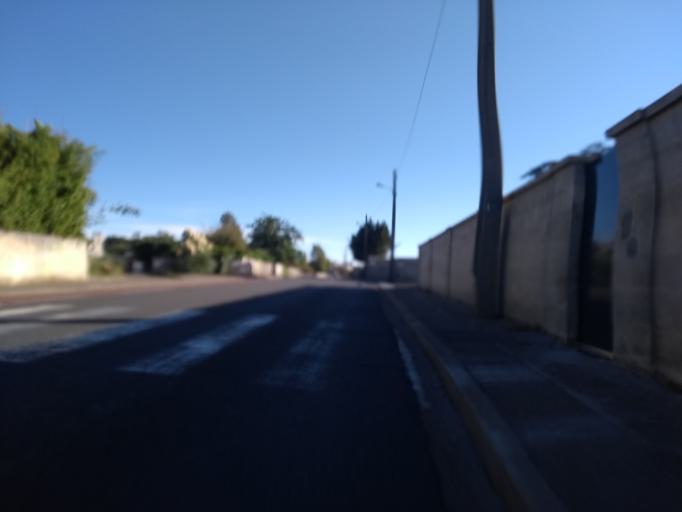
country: FR
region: Aquitaine
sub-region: Departement de la Gironde
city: Talence
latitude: 44.8116
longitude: -0.6005
